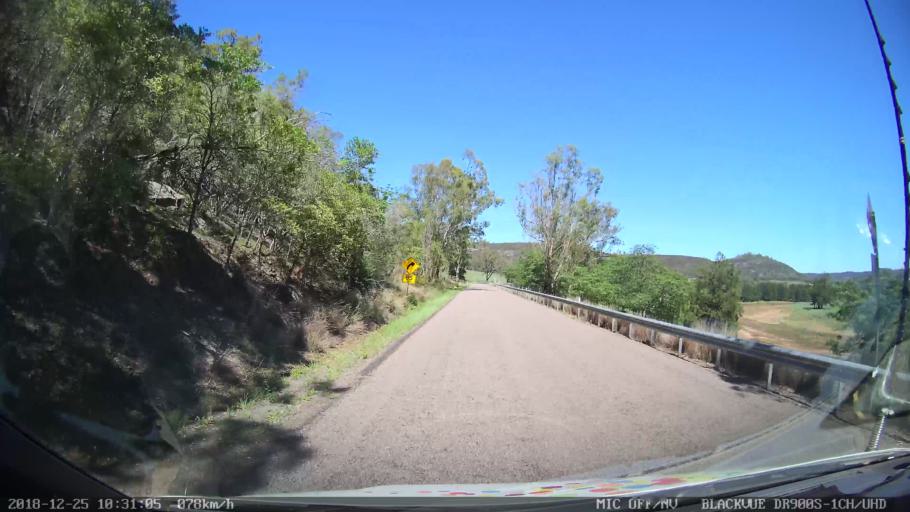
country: AU
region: New South Wales
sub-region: Muswellbrook
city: Denman
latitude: -32.3859
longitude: 150.4318
